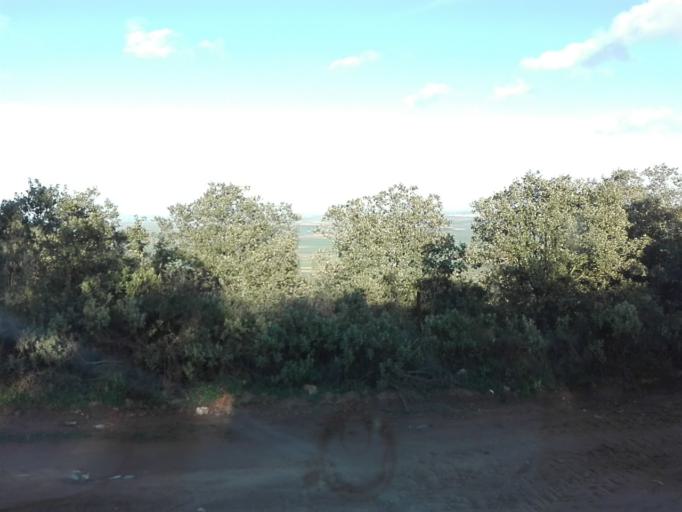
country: ES
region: Extremadura
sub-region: Provincia de Badajoz
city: Trasierra
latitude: 38.2102
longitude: -5.9986
